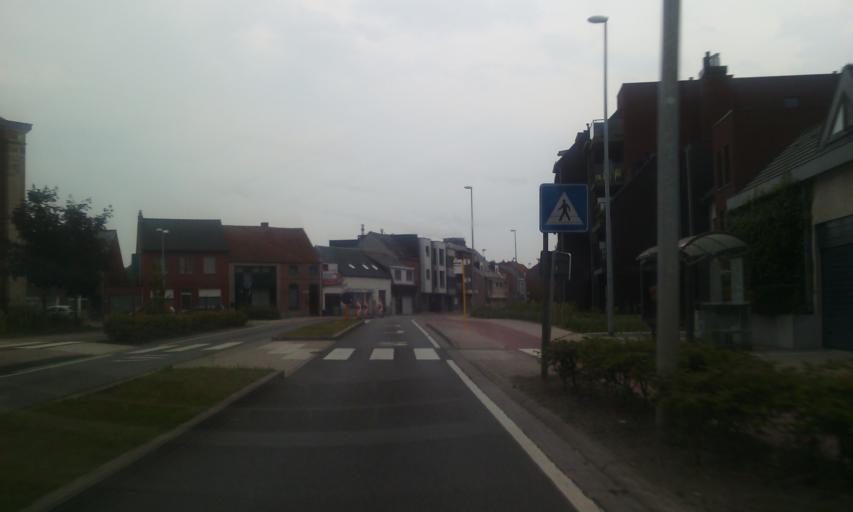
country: BE
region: Flanders
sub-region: Provincie Oost-Vlaanderen
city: Dendermonde
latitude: 51.0543
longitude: 4.1060
